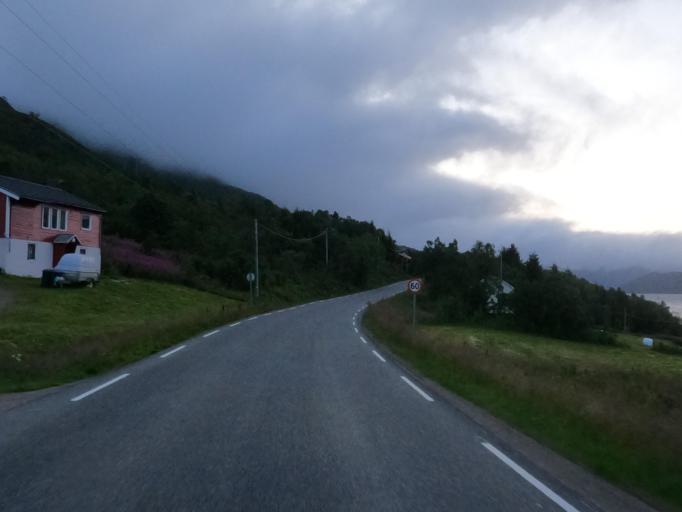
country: NO
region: Nordland
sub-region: Lodingen
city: Lodingen
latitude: 68.5765
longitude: 15.7937
